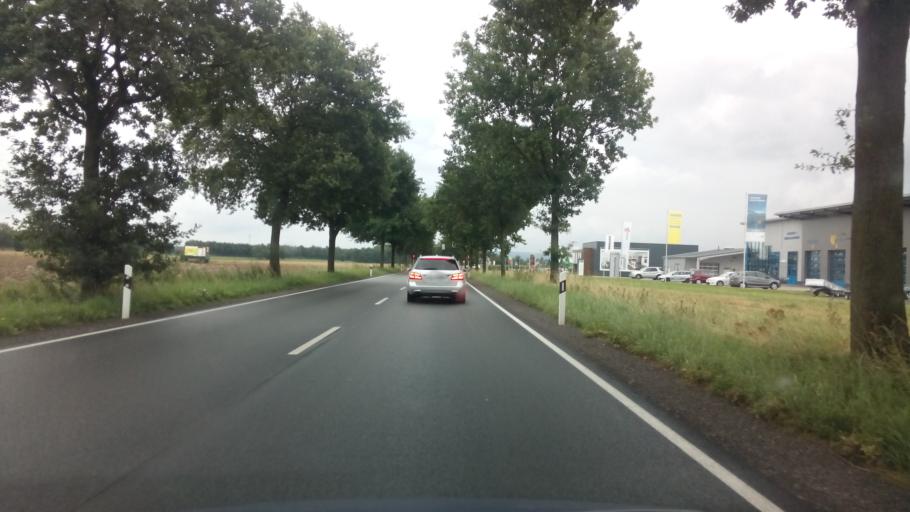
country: DE
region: Lower Saxony
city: Bad Essen
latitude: 52.3299
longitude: 8.3230
